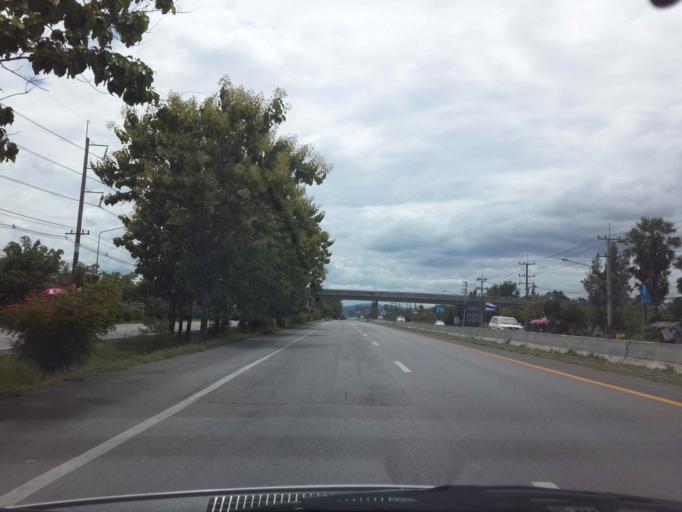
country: TH
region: Phetchaburi
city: Phetchaburi
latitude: 13.1203
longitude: 99.8971
